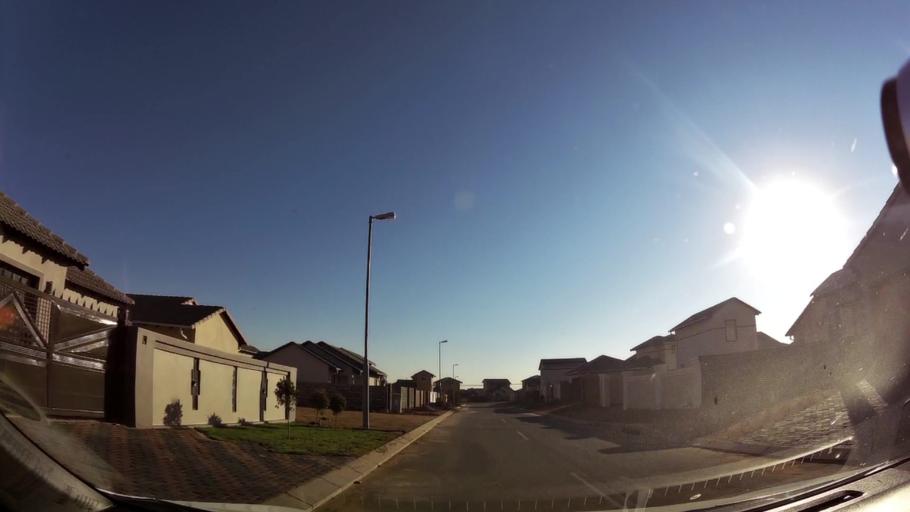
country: ZA
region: Gauteng
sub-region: City of Johannesburg Metropolitan Municipality
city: Midrand
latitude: -25.9275
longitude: 28.1025
